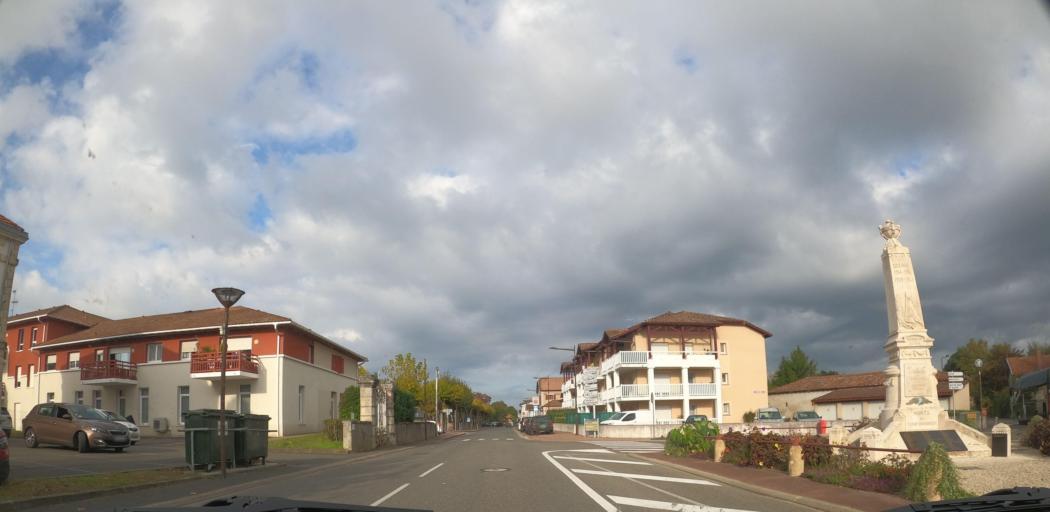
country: FR
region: Aquitaine
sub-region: Departement des Landes
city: Soustons
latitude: 43.7532
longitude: -1.3254
